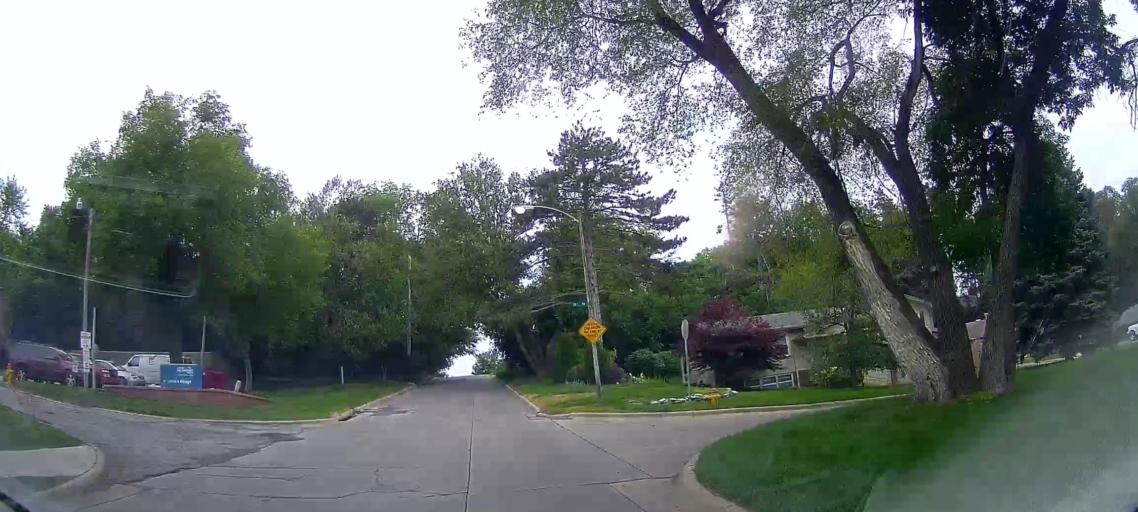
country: US
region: Nebraska
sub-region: Douglas County
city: Ralston
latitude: 41.2670
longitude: -96.0497
